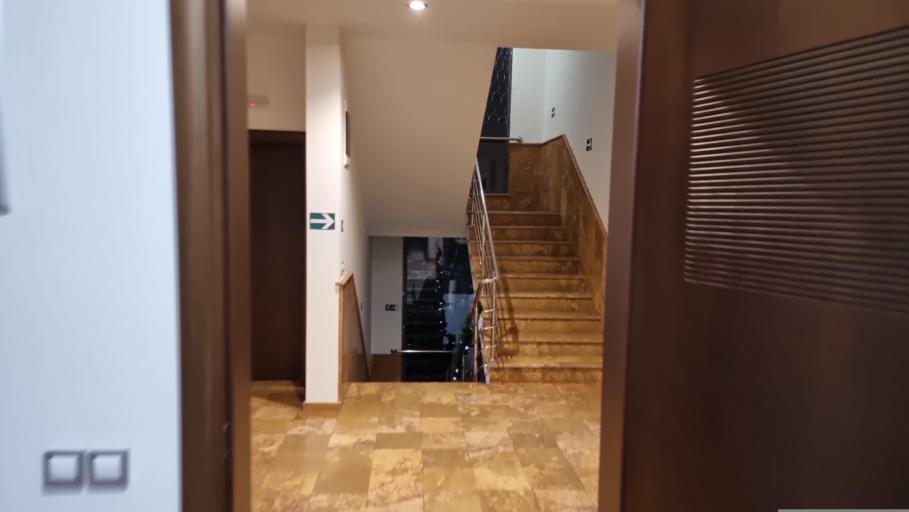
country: MK
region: Kisela Voda
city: Kisela Voda
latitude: 41.9349
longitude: 21.4995
